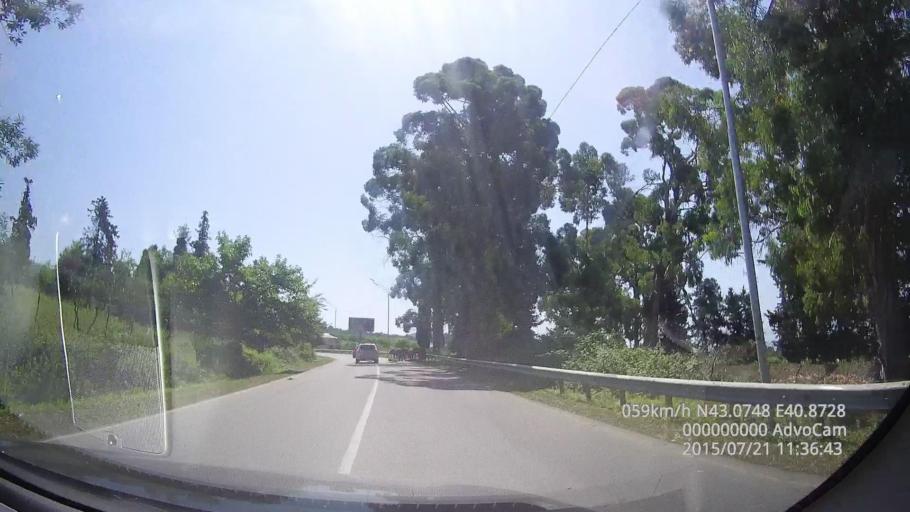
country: GE
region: Abkhazia
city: Stantsiya Novyy Afon
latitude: 43.0745
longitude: 40.8733
